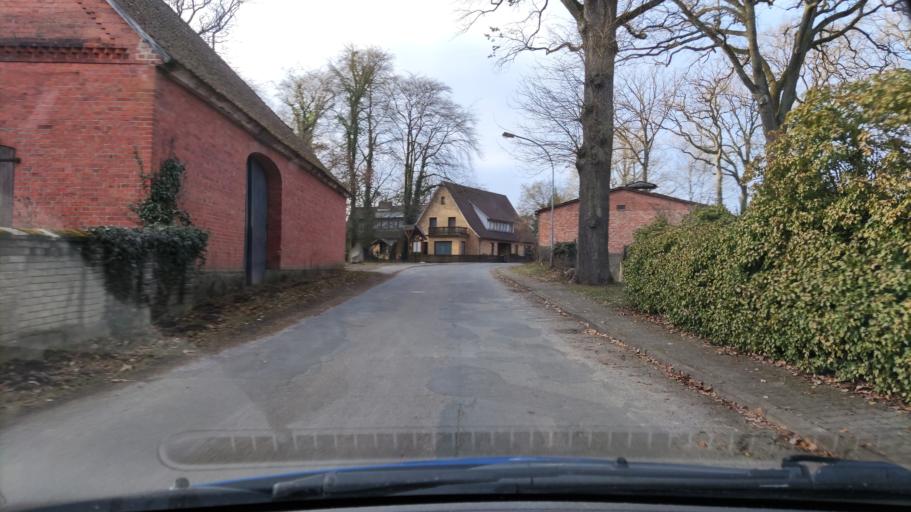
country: DE
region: Lower Saxony
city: Suderburg
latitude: 52.9298
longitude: 10.4412
